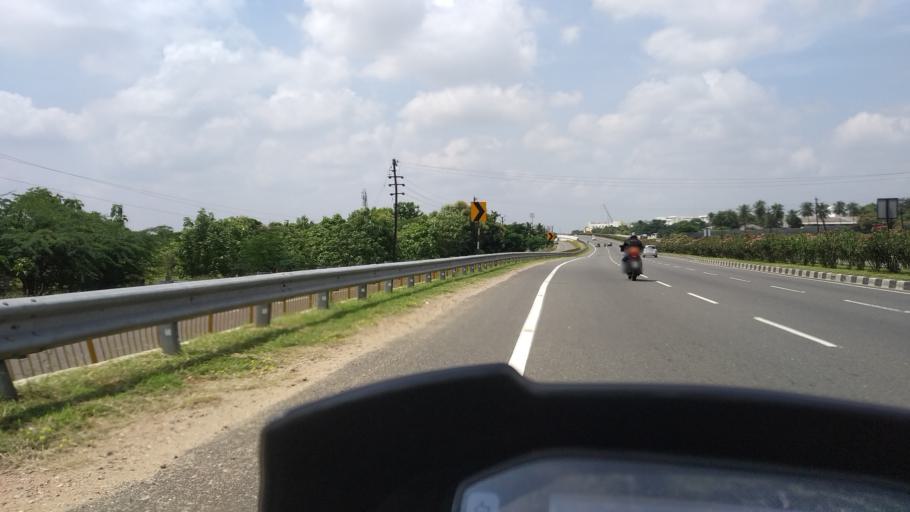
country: IN
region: Tamil Nadu
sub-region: Tiruppur
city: Avinashi
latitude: 11.1705
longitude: 77.2342
